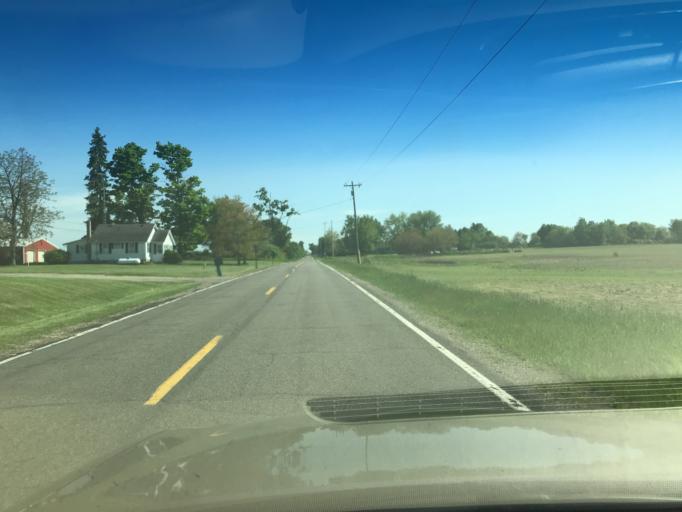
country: US
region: Michigan
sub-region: Ingham County
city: Mason
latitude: 42.5607
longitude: -84.4627
